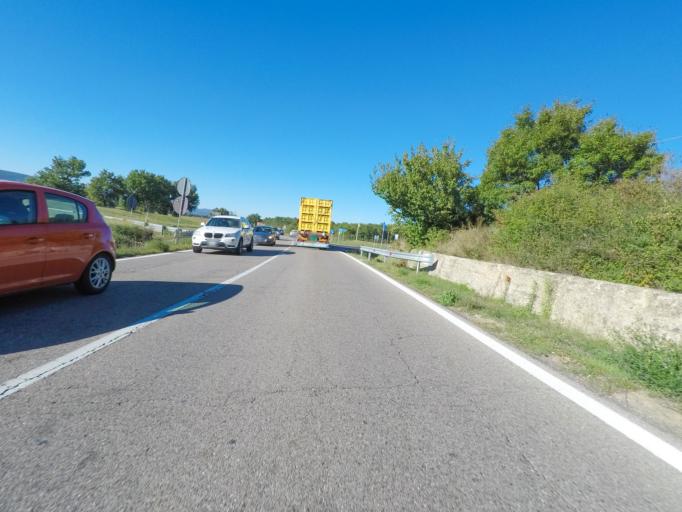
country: IT
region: Tuscany
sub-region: Provincia di Siena
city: Rosia
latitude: 43.2090
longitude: 11.2792
